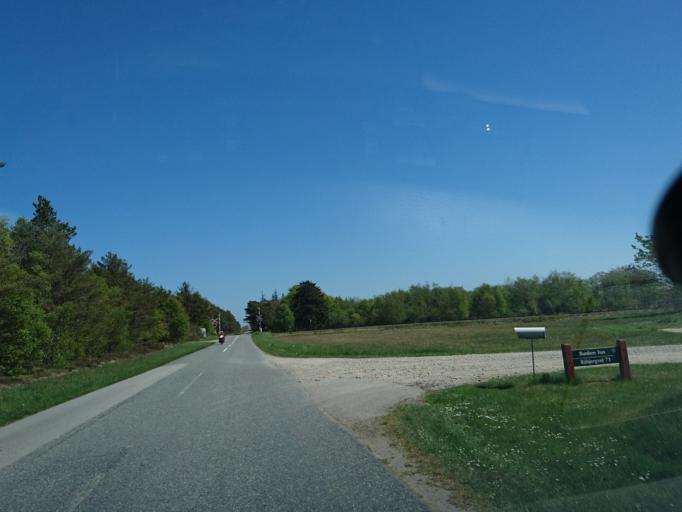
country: DK
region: North Denmark
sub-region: Frederikshavn Kommune
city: Strandby
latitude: 57.6297
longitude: 10.4374
